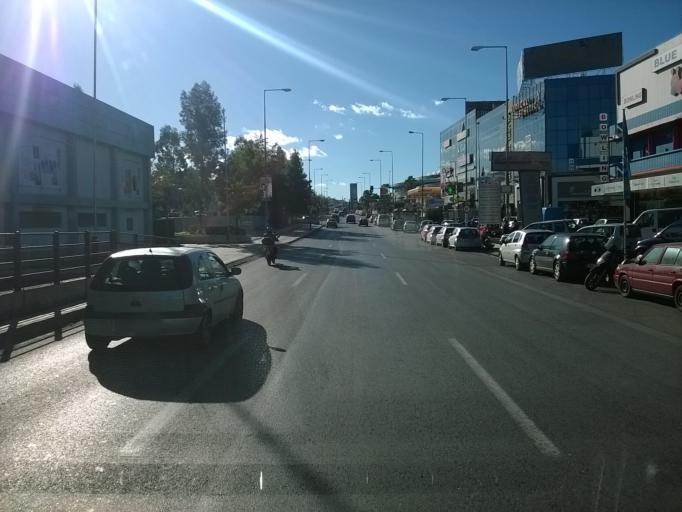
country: GR
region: Attica
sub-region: Nomarchia Athinas
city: Dhafni
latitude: 37.9416
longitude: 23.7402
